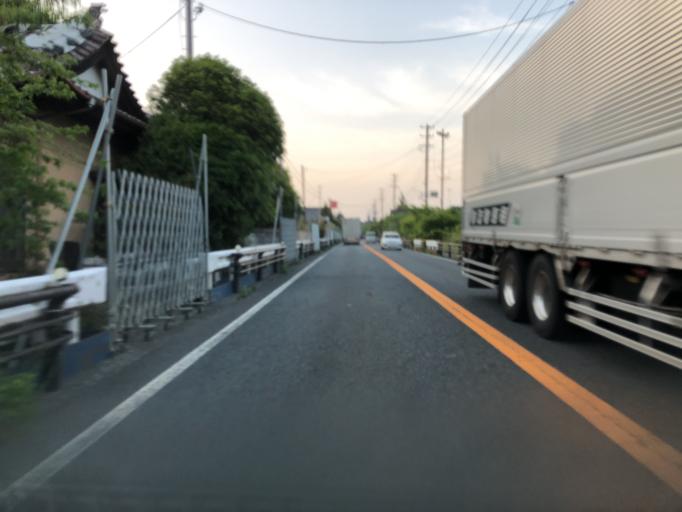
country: JP
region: Fukushima
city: Namie
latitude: 37.3815
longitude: 141.0087
